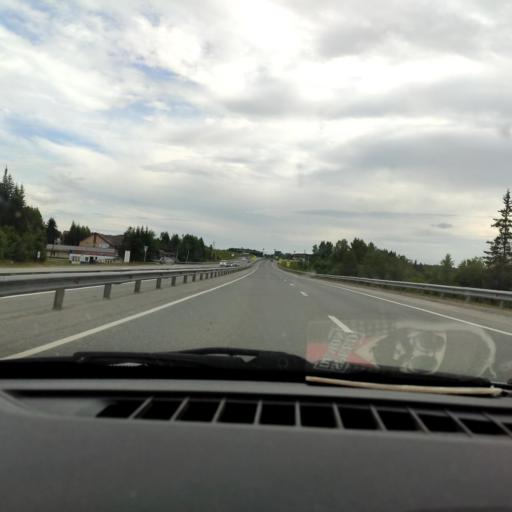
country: RU
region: Perm
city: Polazna
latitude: 58.2714
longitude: 56.4151
